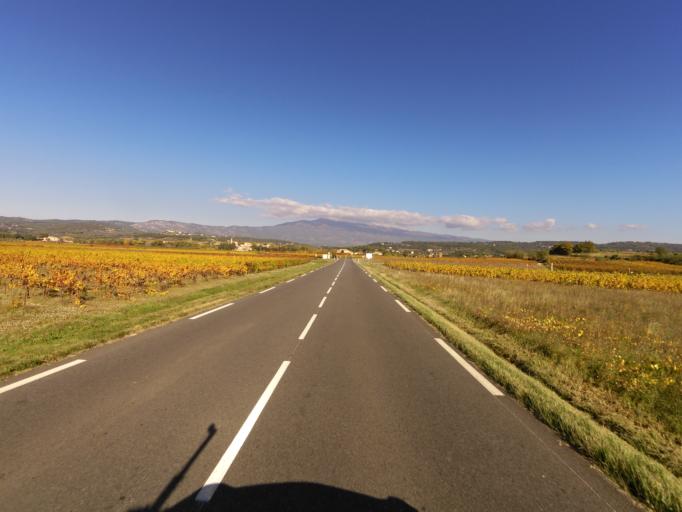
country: FR
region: Provence-Alpes-Cote d'Azur
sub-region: Departement du Vaucluse
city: Caromb
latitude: 44.0915
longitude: 5.1290
